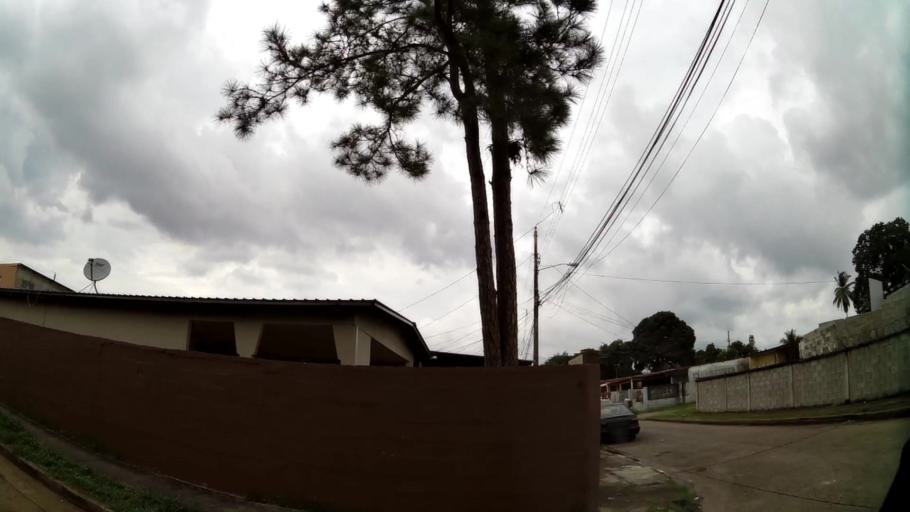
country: PA
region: Panama
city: Tocumen
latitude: 9.0554
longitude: -79.4084
